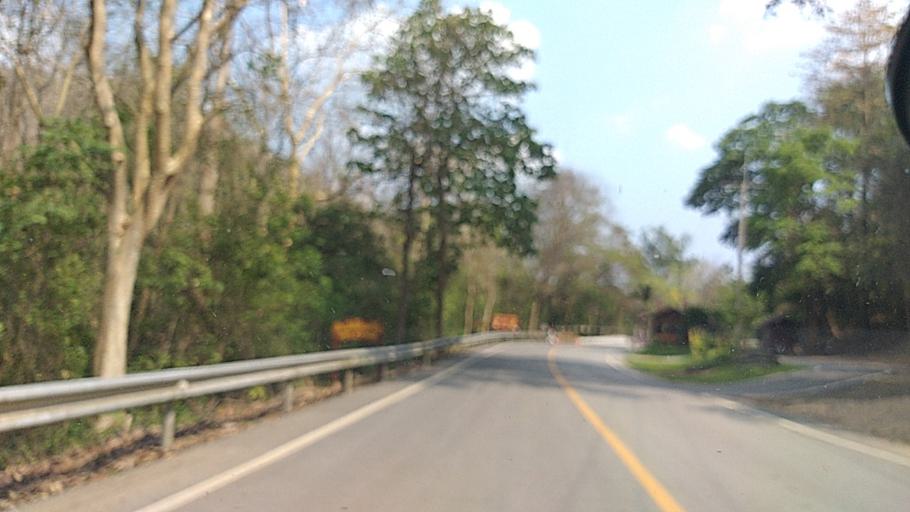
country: TH
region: Sara Buri
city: Saraburi
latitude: 14.4453
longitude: 100.9569
